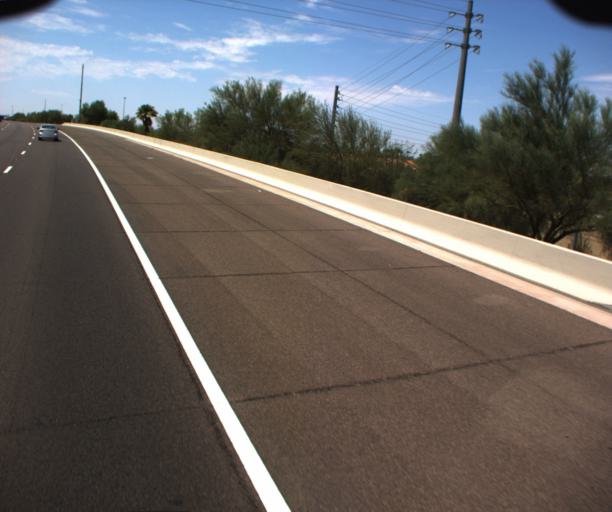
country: US
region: Arizona
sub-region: Maricopa County
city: Guadalupe
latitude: 33.3873
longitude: -111.9596
